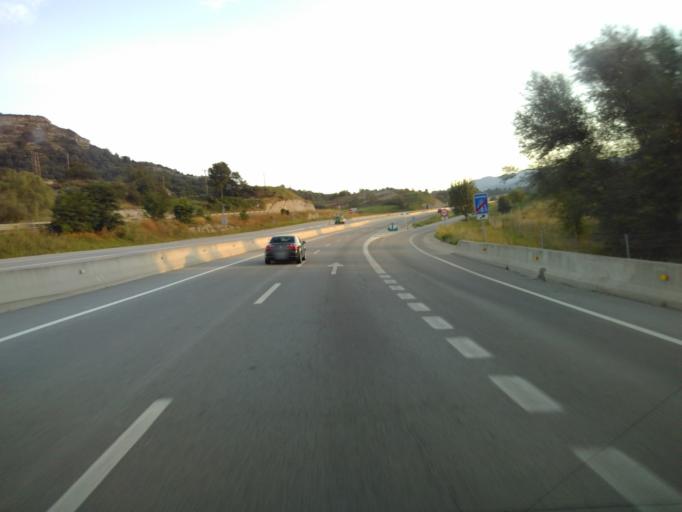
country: ES
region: Catalonia
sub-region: Provincia de Barcelona
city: Oris
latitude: 42.0447
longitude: 2.2324
